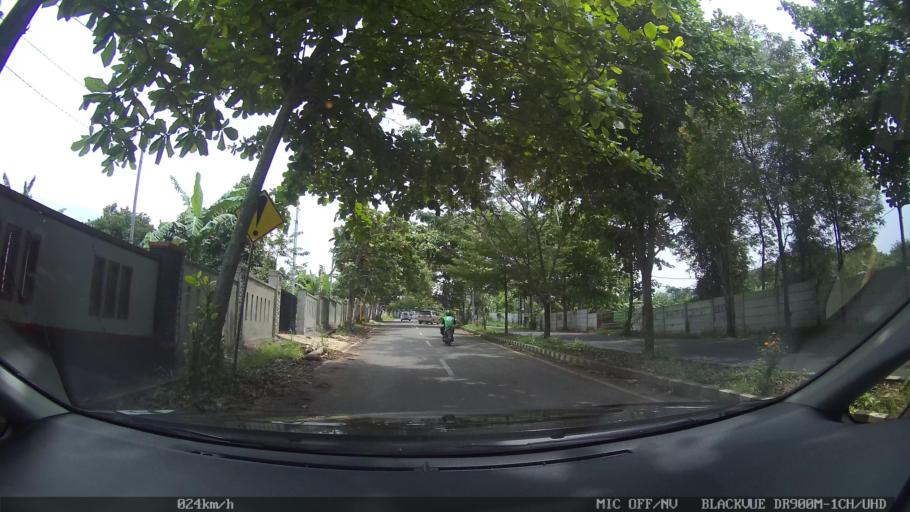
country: ID
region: Lampung
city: Bandarlampung
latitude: -5.4361
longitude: 105.2485
